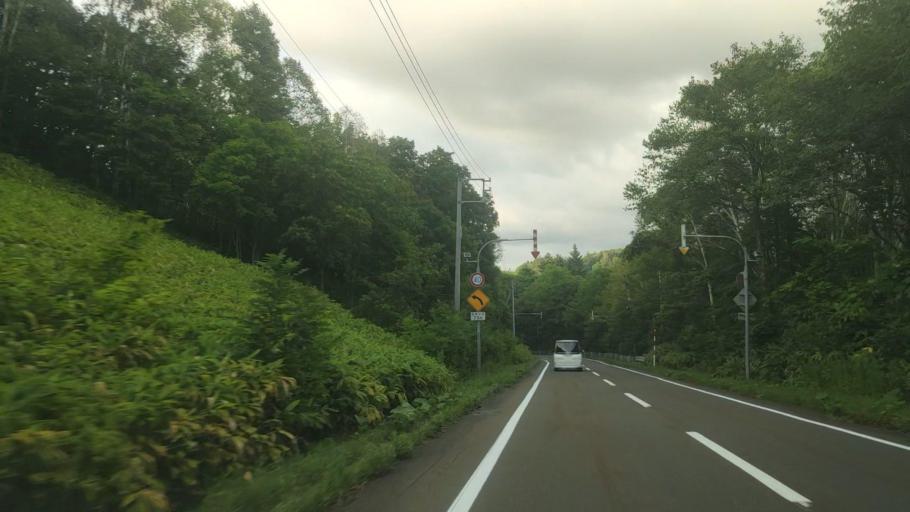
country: JP
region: Hokkaido
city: Bibai
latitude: 43.1699
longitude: 142.0724
